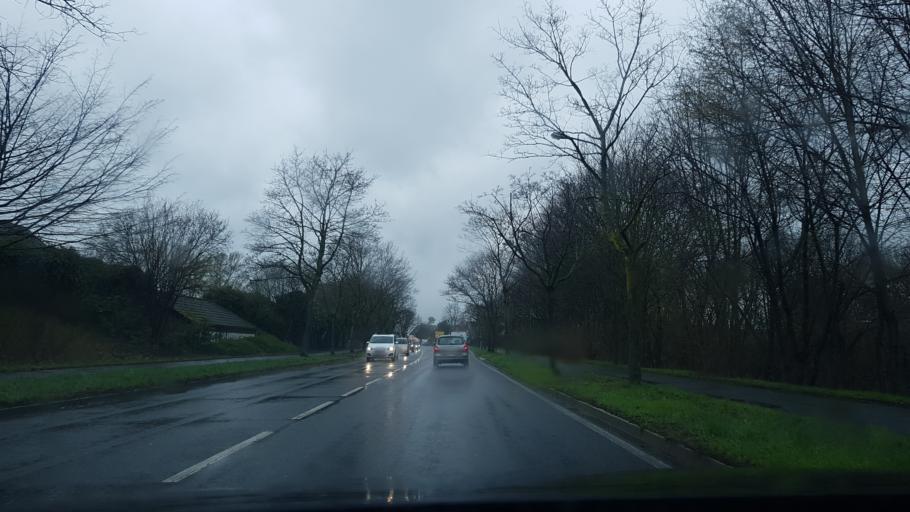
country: DE
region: North Rhine-Westphalia
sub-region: Regierungsbezirk Dusseldorf
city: Langenfeld
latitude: 51.1138
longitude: 6.9407
